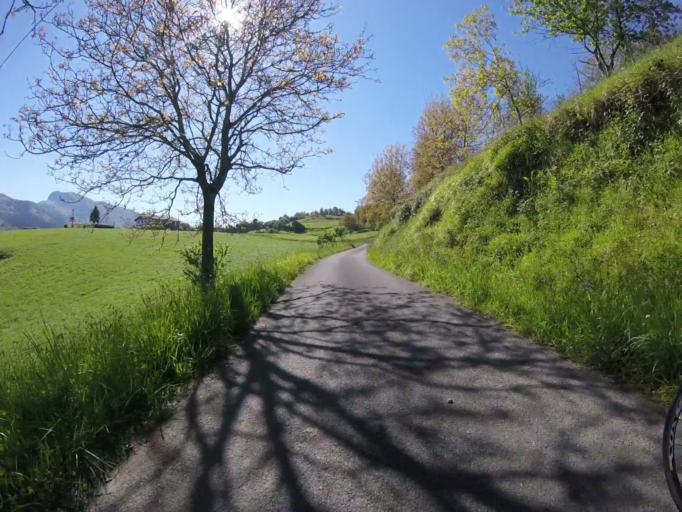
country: ES
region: Basque Country
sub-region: Provincia de Guipuzcoa
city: Errezil
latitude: 43.1693
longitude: -2.2080
